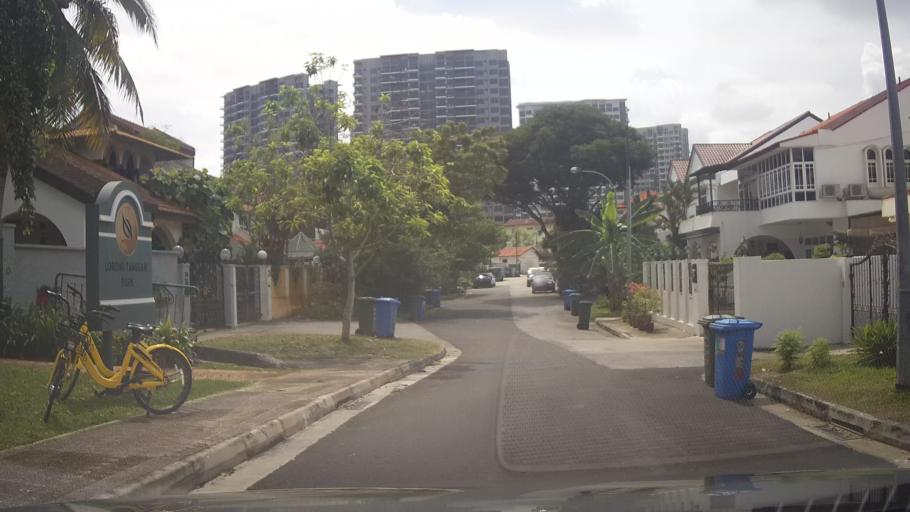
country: MY
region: Johor
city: Kampung Pasir Gudang Baru
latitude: 1.3989
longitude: 103.8735
